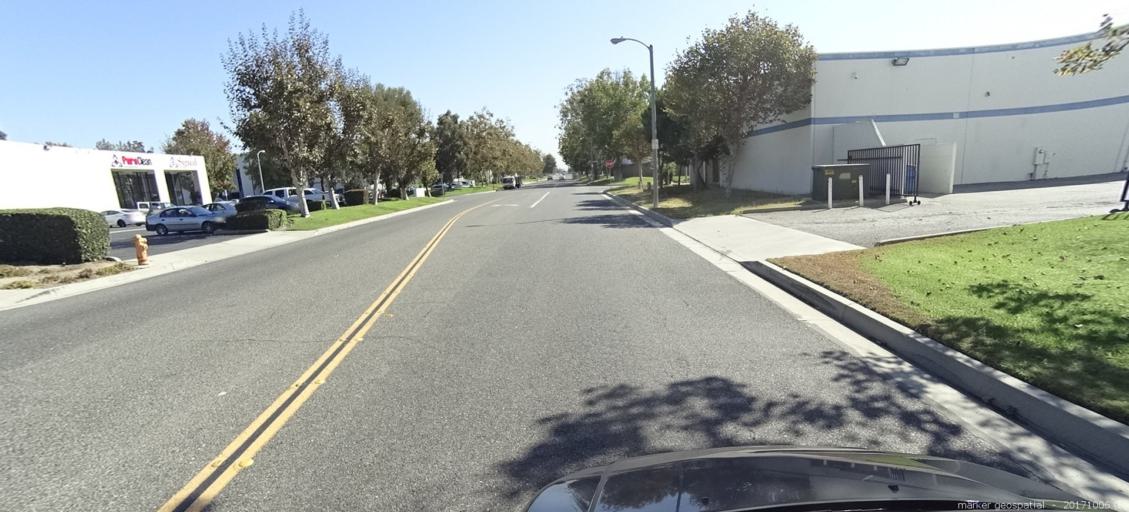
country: US
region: California
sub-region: Orange County
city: Stanton
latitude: 33.7955
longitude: -118.0076
